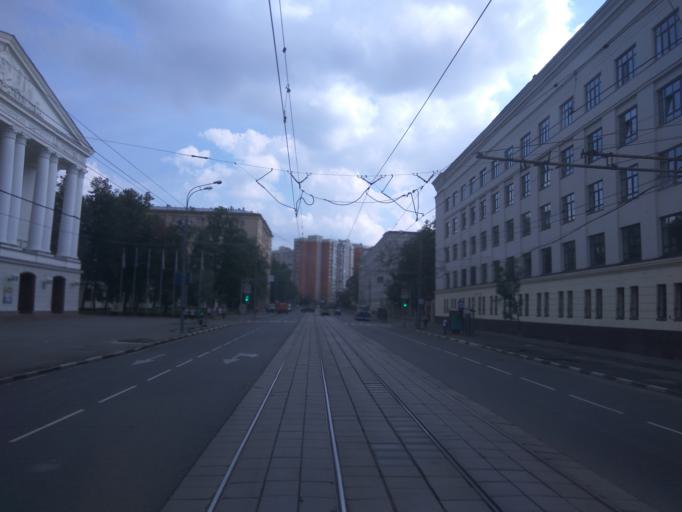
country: RU
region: Moscow
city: Lefortovo
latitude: 55.7547
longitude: 37.7072
